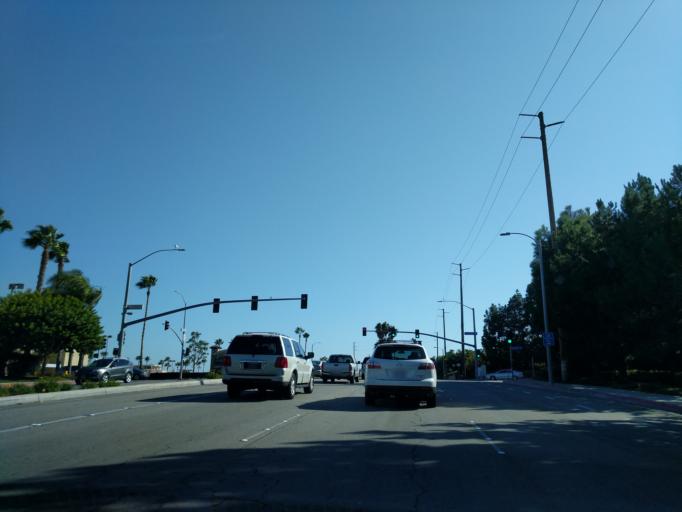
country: US
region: California
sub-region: Orange County
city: Huntington Beach
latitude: 33.6837
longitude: -118.0063
